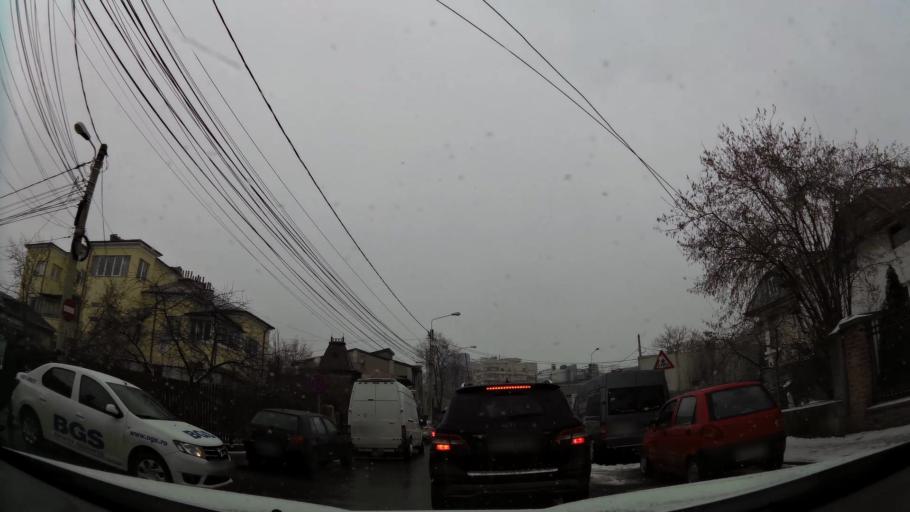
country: RO
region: Prahova
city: Ploiesti
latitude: 44.9409
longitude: 26.0152
